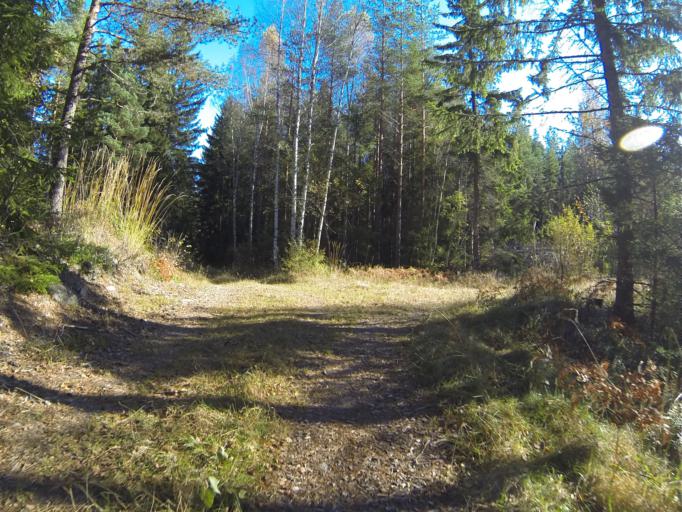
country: FI
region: Varsinais-Suomi
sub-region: Salo
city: Saerkisalo
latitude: 60.2076
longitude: 22.9573
